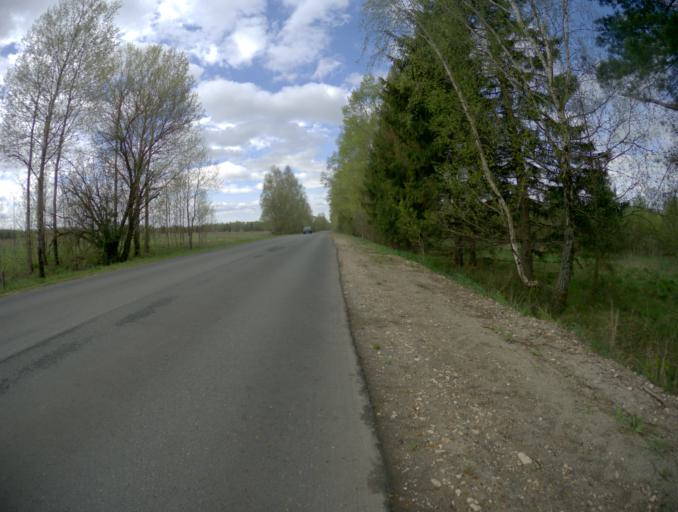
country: RU
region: Vladimir
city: Golovino
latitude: 55.9621
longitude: 40.5149
